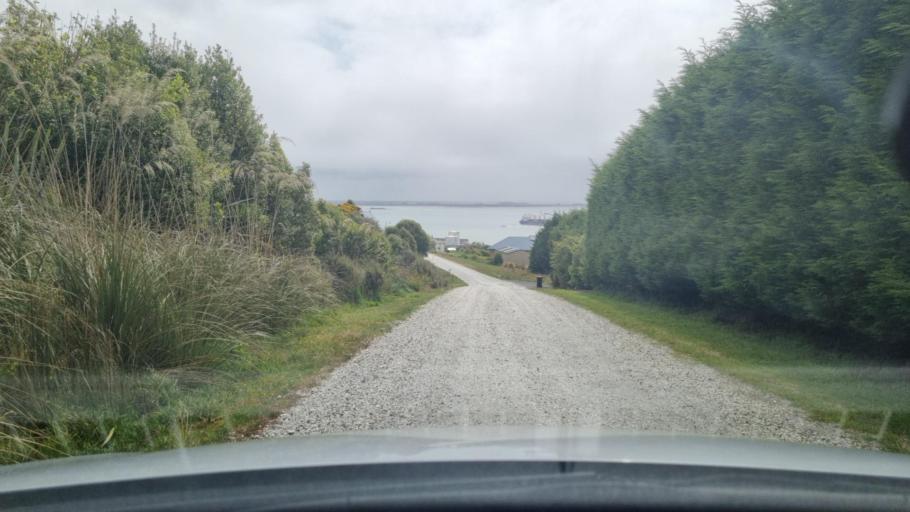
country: NZ
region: Southland
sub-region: Invercargill City
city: Bluff
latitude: -46.6094
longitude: 168.3519
